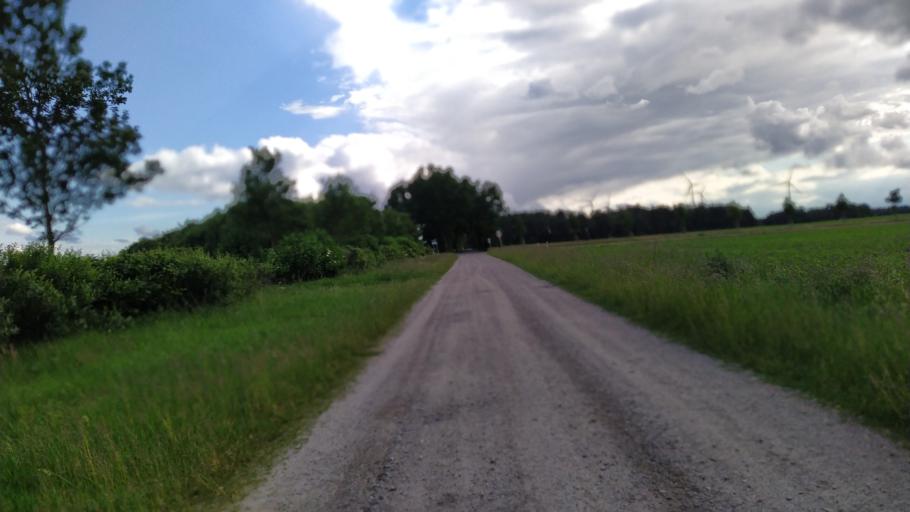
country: DE
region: Lower Saxony
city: Sandbostel
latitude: 53.4319
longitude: 9.1719
